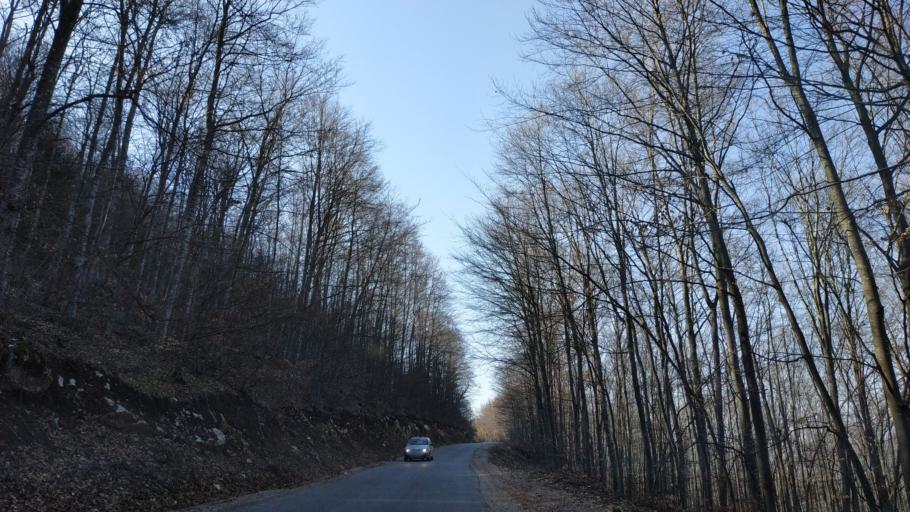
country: RS
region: Central Serbia
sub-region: Zajecarski Okrug
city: Soko Banja
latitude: 43.5981
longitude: 21.8883
